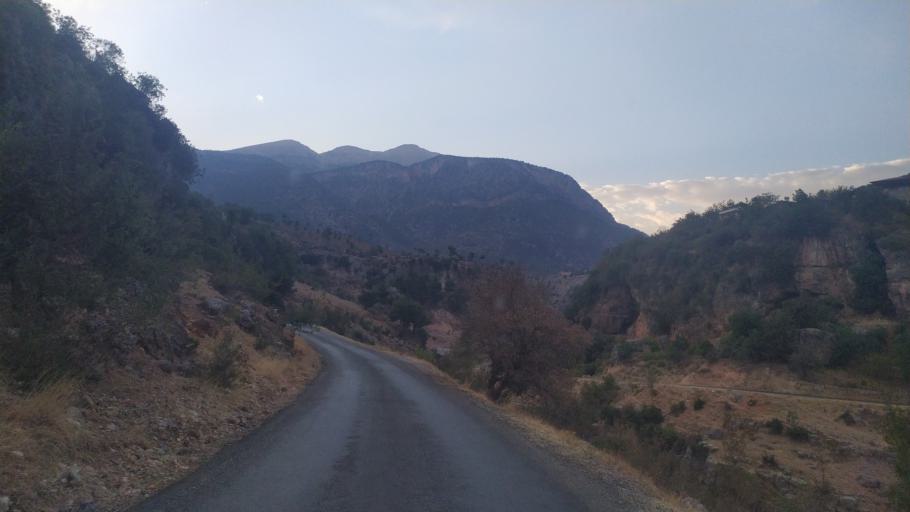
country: TR
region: Mersin
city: Camliyayla
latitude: 37.2374
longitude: 34.7170
